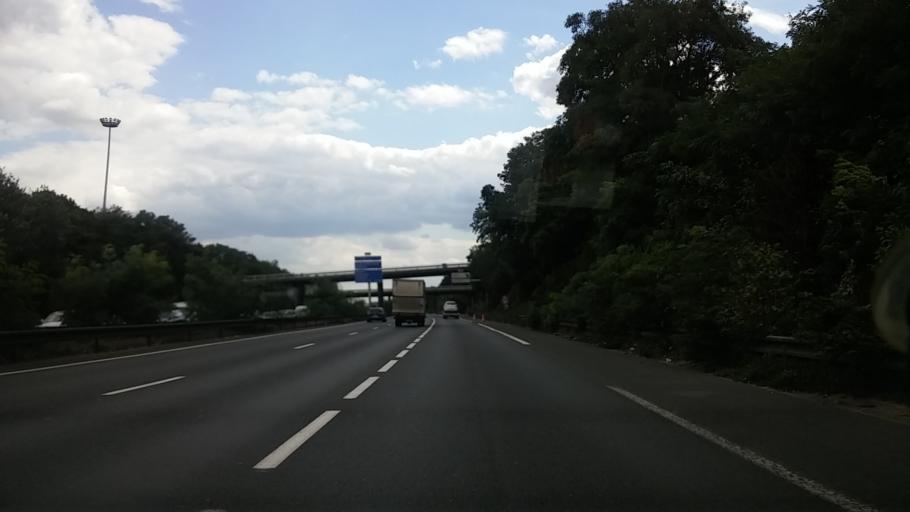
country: FR
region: Ile-de-France
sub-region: Departement de Seine-Saint-Denis
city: Le Blanc-Mesnil
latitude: 48.9523
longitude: 2.4737
